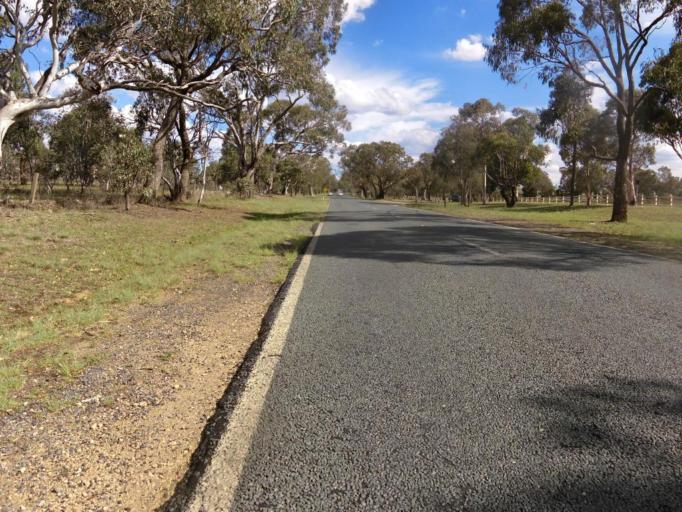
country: AU
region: Australian Capital Territory
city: Belconnen
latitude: -35.1782
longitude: 149.0726
